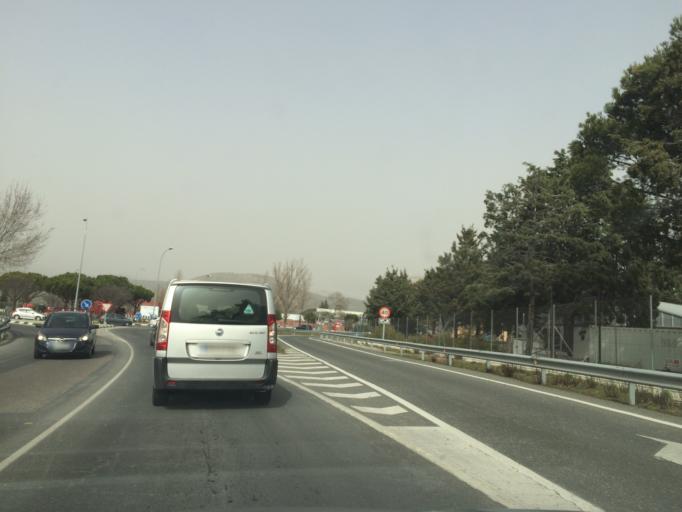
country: ES
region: Madrid
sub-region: Provincia de Madrid
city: Collado-Villalba
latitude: 40.6396
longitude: -4.0055
